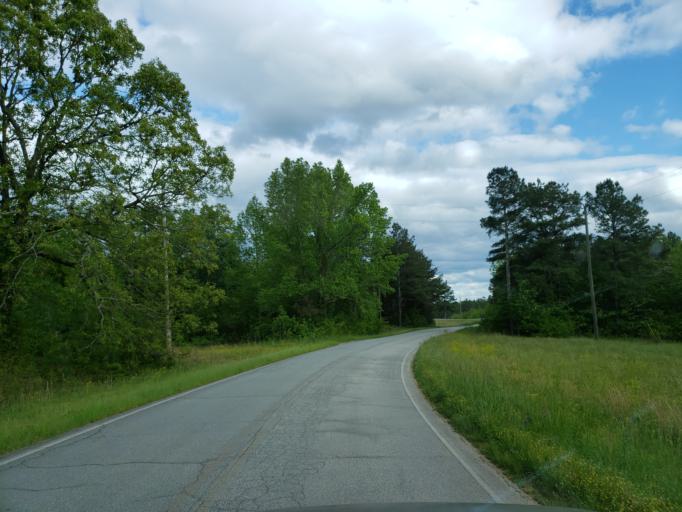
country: US
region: Georgia
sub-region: Haralson County
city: Tallapoosa
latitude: 33.7932
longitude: -85.3454
